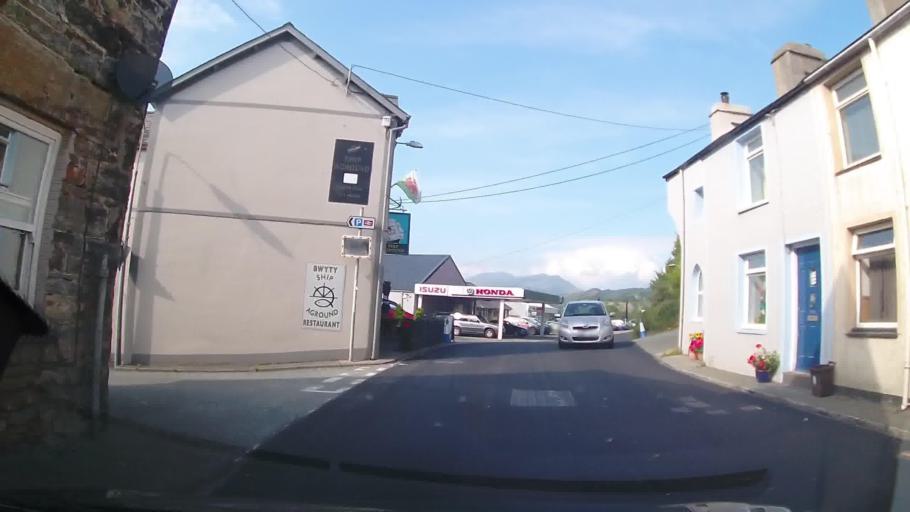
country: GB
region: Wales
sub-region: Gwynedd
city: Penrhyndeudraeth
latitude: 52.9036
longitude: -4.0648
